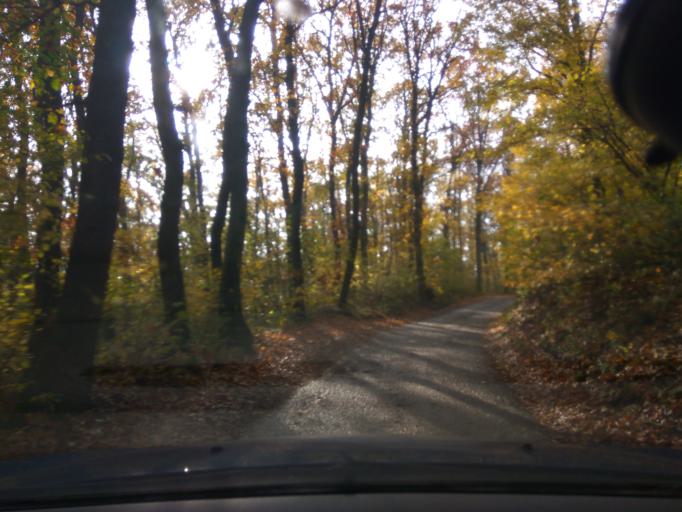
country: SK
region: Trnavsky
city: Vrbove
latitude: 48.6817
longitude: 17.7133
